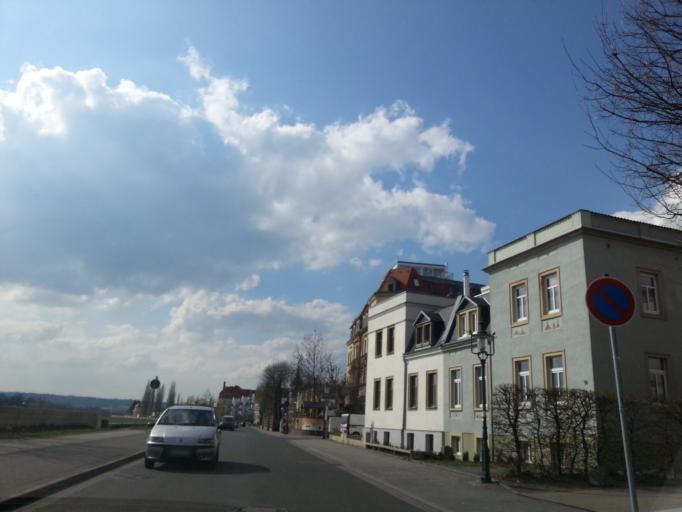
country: DE
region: Saxony
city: Dresden
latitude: 51.0775
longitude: 13.7135
